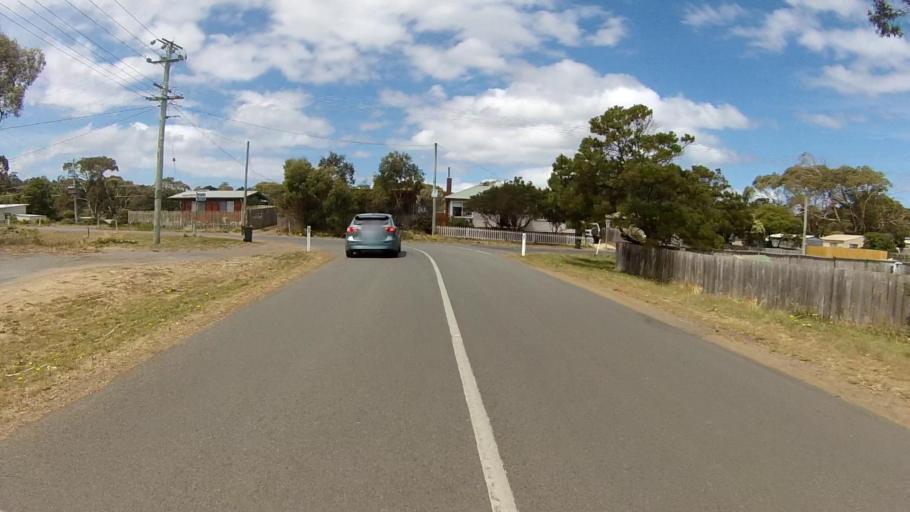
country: AU
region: Tasmania
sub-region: Sorell
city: Sorell
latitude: -42.8707
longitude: 147.6369
